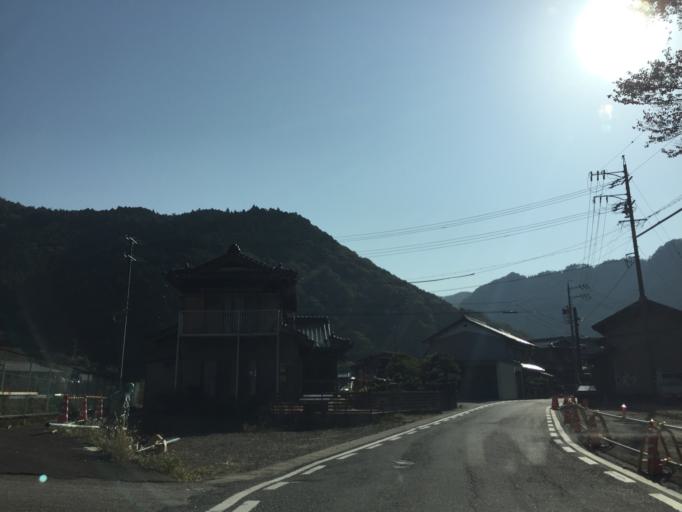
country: JP
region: Gifu
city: Minokamo
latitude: 35.5449
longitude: 137.1201
